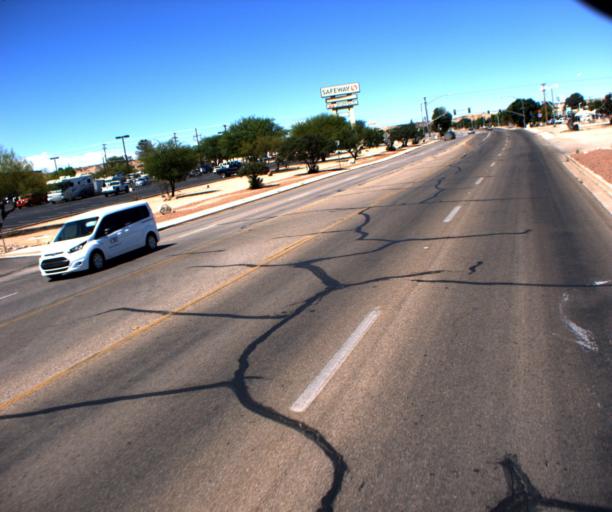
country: US
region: Arizona
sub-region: Cochise County
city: Benson
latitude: 31.9702
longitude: -110.3052
